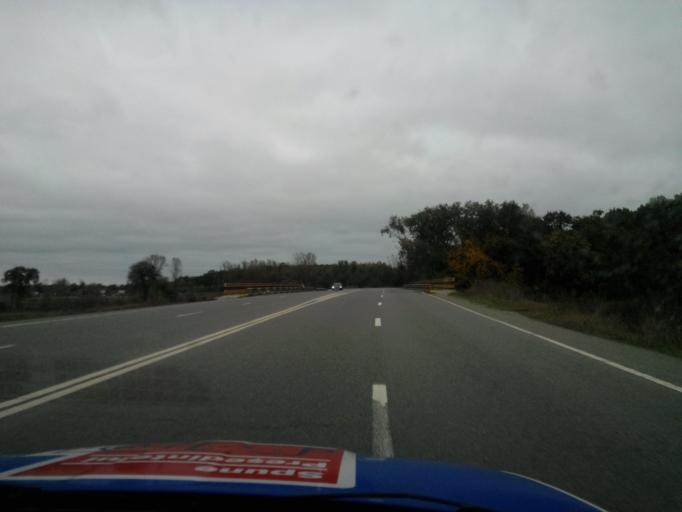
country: RO
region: Giurgiu
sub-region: Comuna Calugareni
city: Calugareni
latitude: 44.1624
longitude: 25.9988
